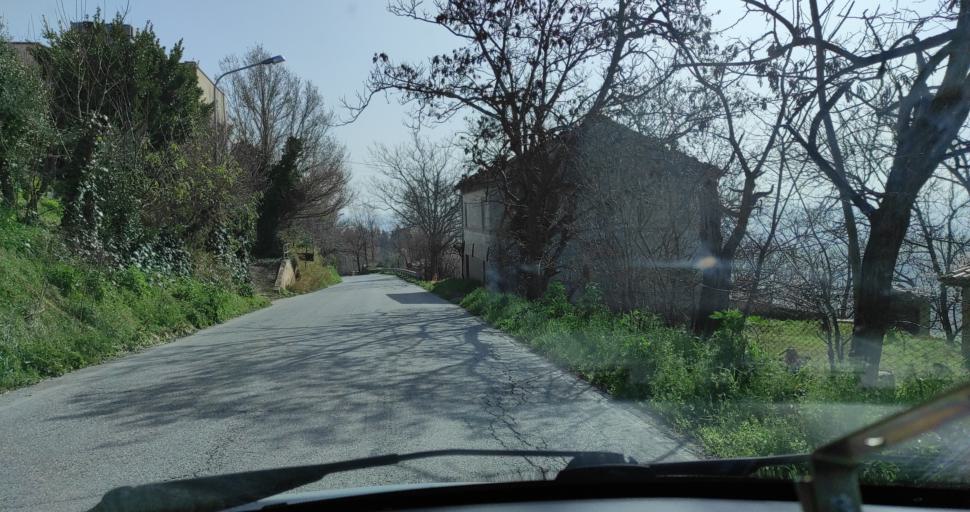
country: IT
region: The Marches
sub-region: Provincia di Macerata
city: Loro Piceno
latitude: 43.1645
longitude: 13.4186
